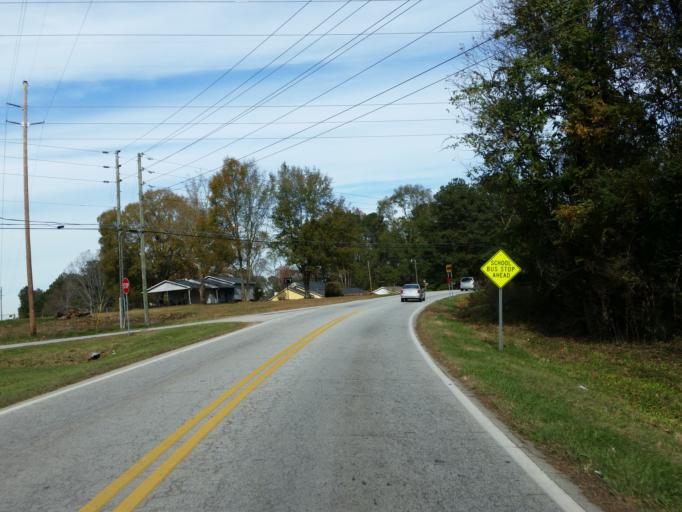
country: US
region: Georgia
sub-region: Douglas County
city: Lithia Springs
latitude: 33.7399
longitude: -84.6672
